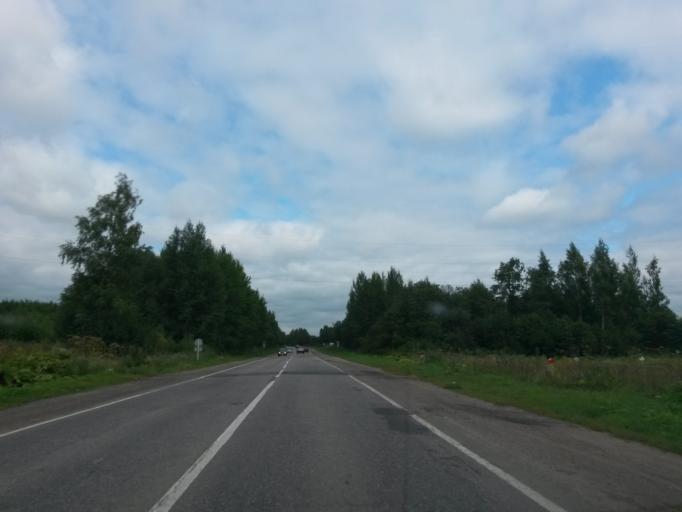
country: RU
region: Jaroslavl
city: Yaroslavl
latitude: 57.5326
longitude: 39.8741
